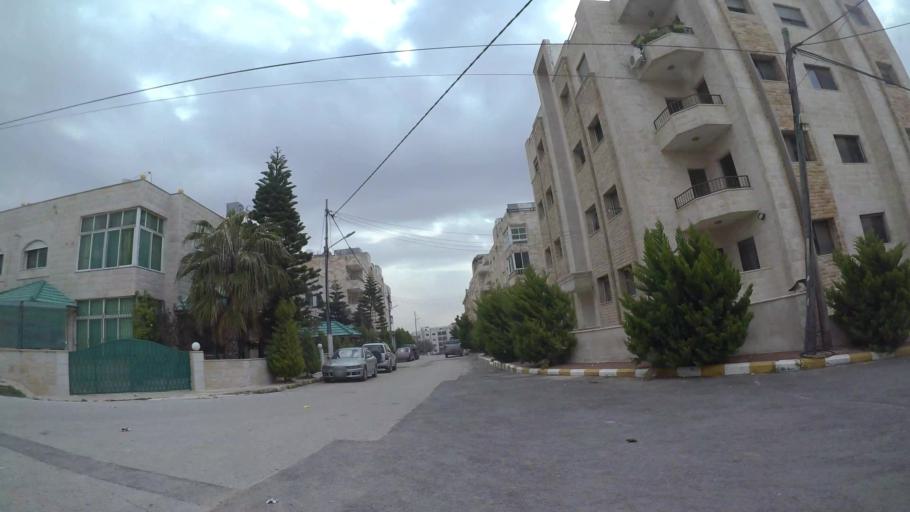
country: JO
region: Amman
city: Umm as Summaq
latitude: 31.8958
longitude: 35.8424
